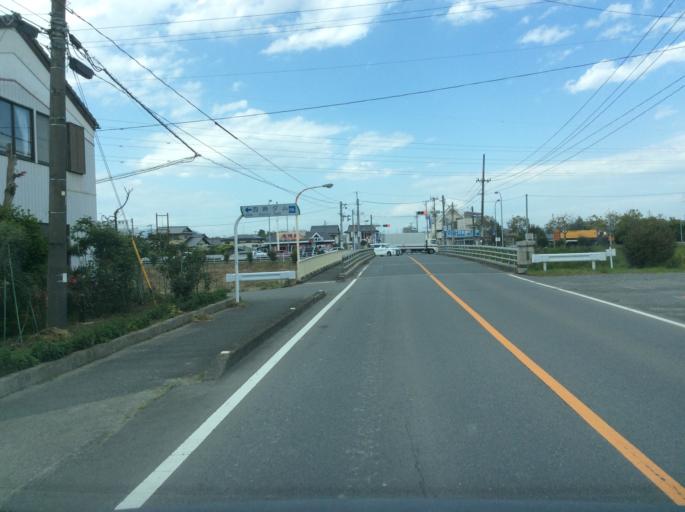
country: JP
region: Ibaraki
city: Kitaibaraki
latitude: 36.8947
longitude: 140.7826
